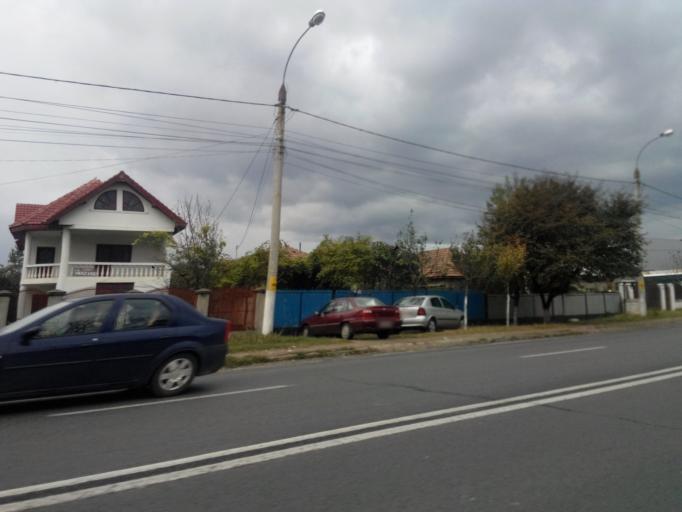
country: RO
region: Buzau
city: Buzau
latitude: 45.1788
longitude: 26.8279
